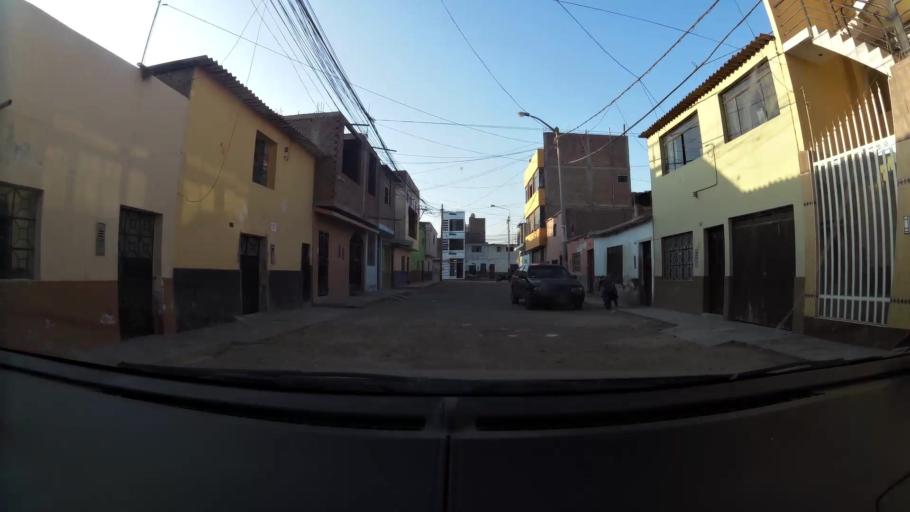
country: PE
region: Lambayeque
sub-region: Provincia de Chiclayo
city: Santa Rosa
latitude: -6.7688
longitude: -79.8292
